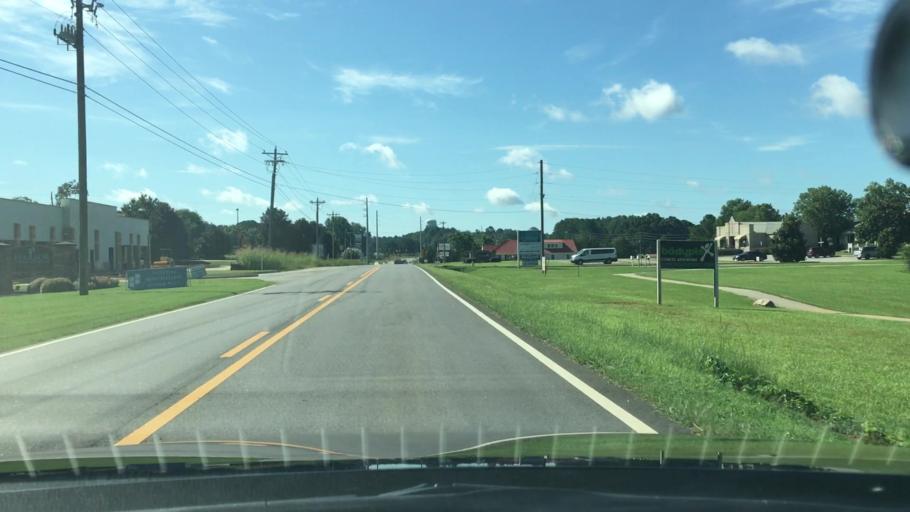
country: US
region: Georgia
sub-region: Putnam County
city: Jefferson
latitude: 33.4241
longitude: -83.2708
